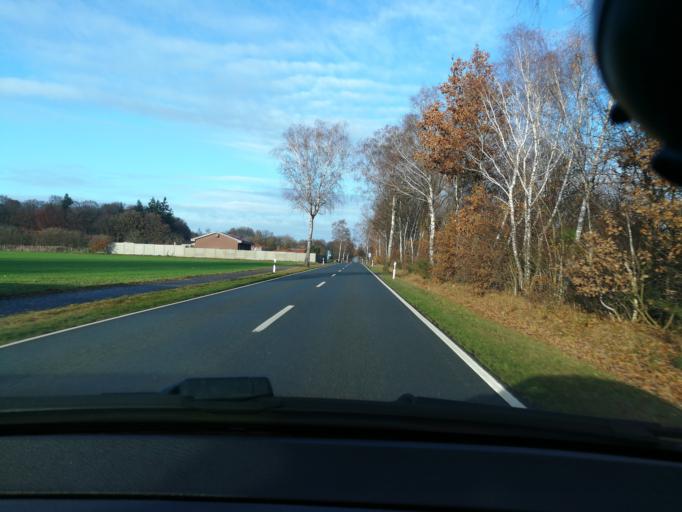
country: DE
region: Lower Saxony
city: Schwaforden
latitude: 52.7233
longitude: 8.8153
